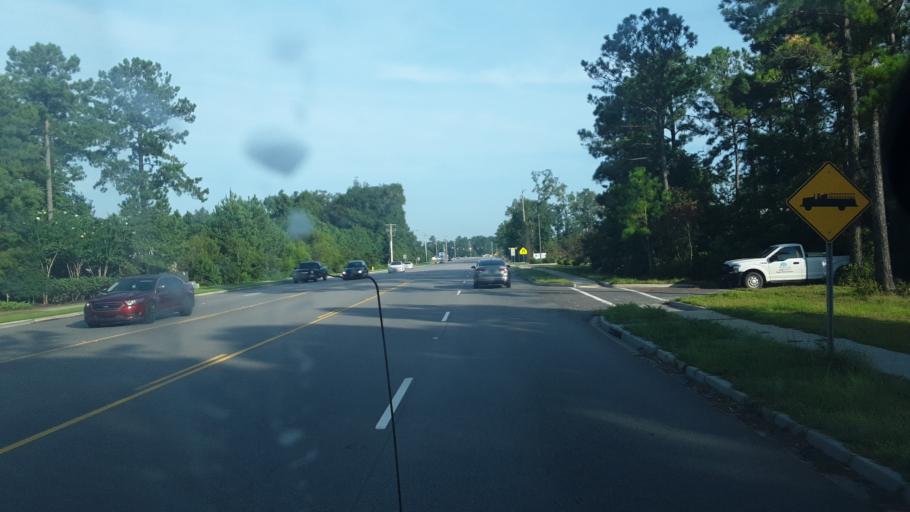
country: US
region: South Carolina
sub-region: Horry County
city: Myrtle Beach
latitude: 33.7635
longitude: -78.8622
